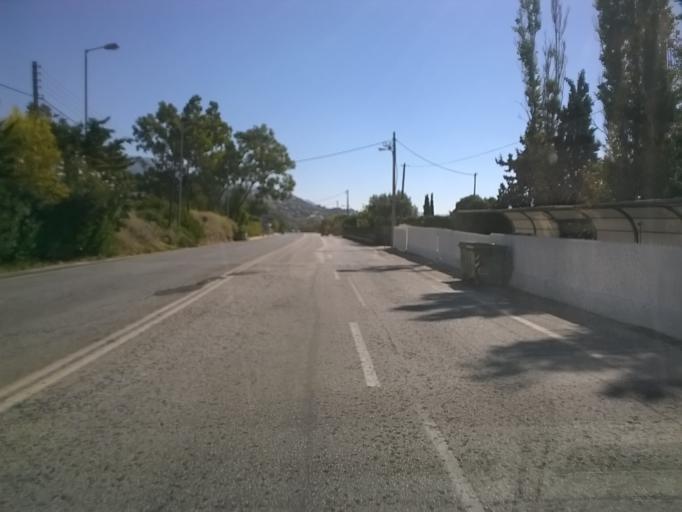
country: GR
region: Attica
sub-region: Nomarchia Anatolikis Attikis
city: Agios Dimitrios Kropias
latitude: 37.8043
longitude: 23.8563
